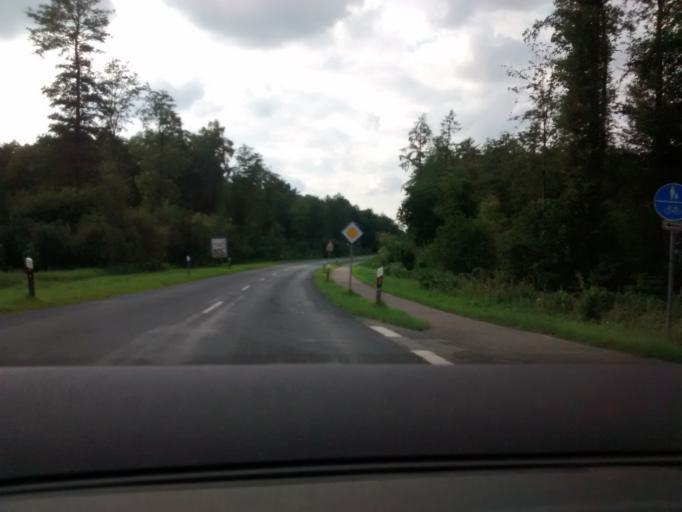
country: DE
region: Lower Saxony
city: Scharnebeck
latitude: 53.3146
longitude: 10.4871
